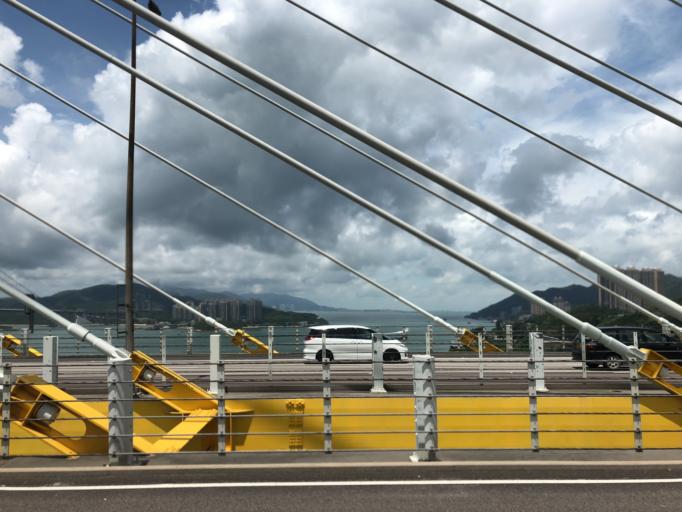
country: HK
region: Tsuen Wan
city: Tsuen Wan
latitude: 22.3659
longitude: 114.0788
